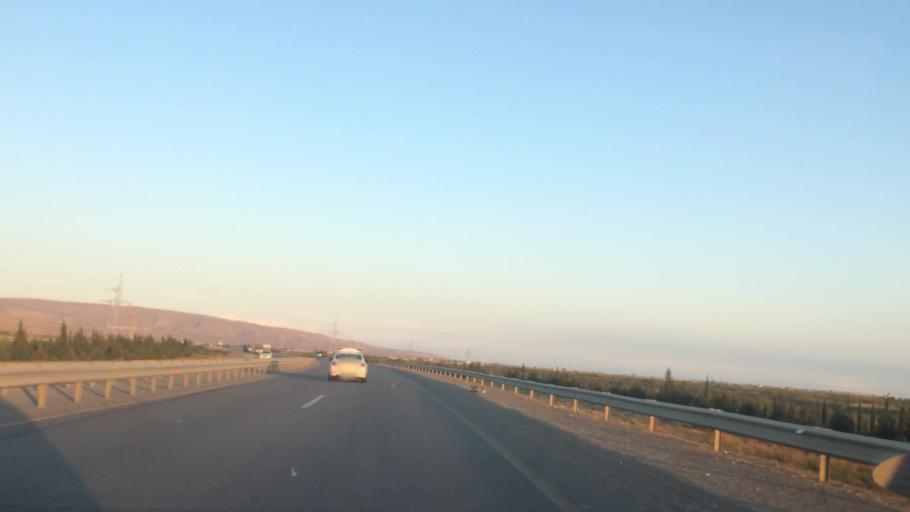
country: AZ
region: Baki
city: Qobustan
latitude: 39.9823
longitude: 49.2191
